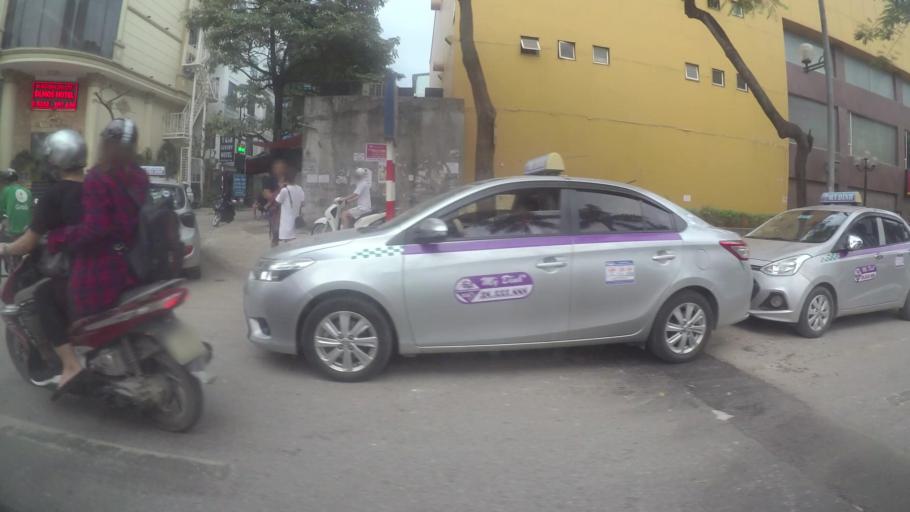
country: VN
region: Ha Noi
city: Cau Dien
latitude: 21.0288
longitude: 105.7688
